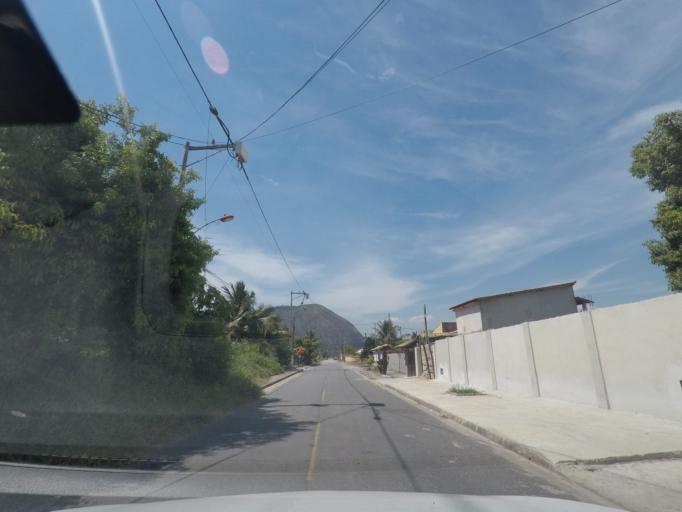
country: BR
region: Rio de Janeiro
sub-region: Marica
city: Marica
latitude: -22.9605
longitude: -42.9604
